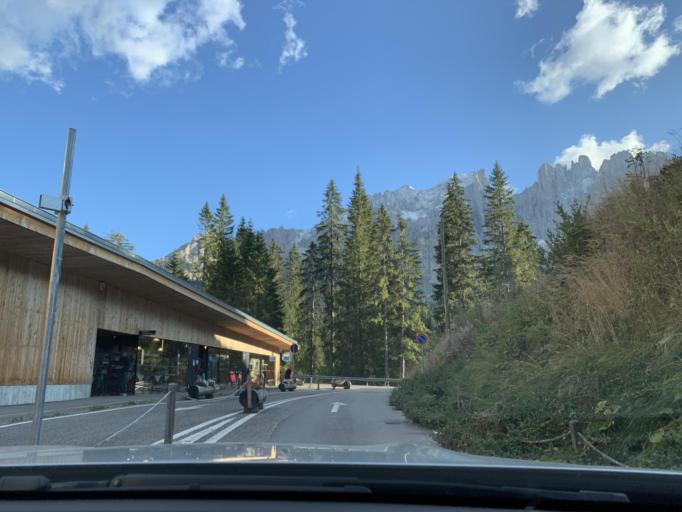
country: IT
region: Trentino-Alto Adige
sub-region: Bolzano
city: Nova Levante
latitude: 46.4110
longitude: 11.5754
